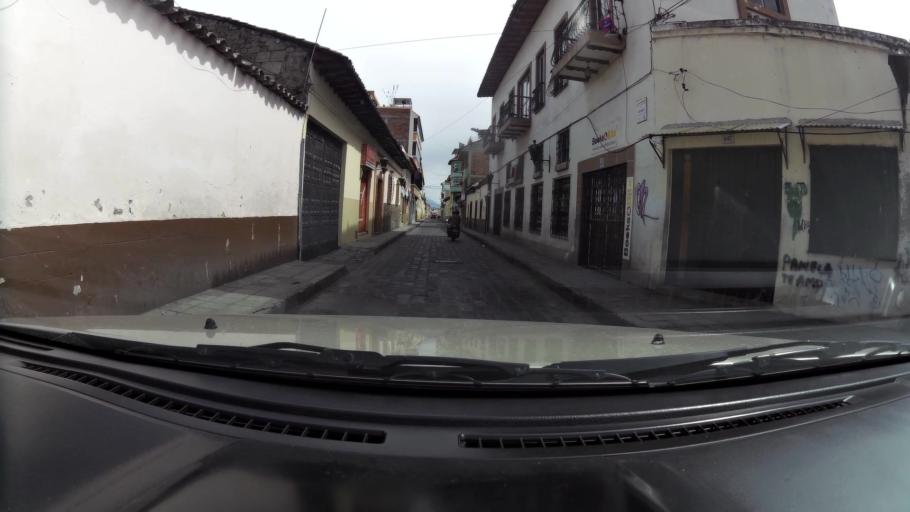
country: EC
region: Cotopaxi
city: Latacunga
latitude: -0.9285
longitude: -78.6094
